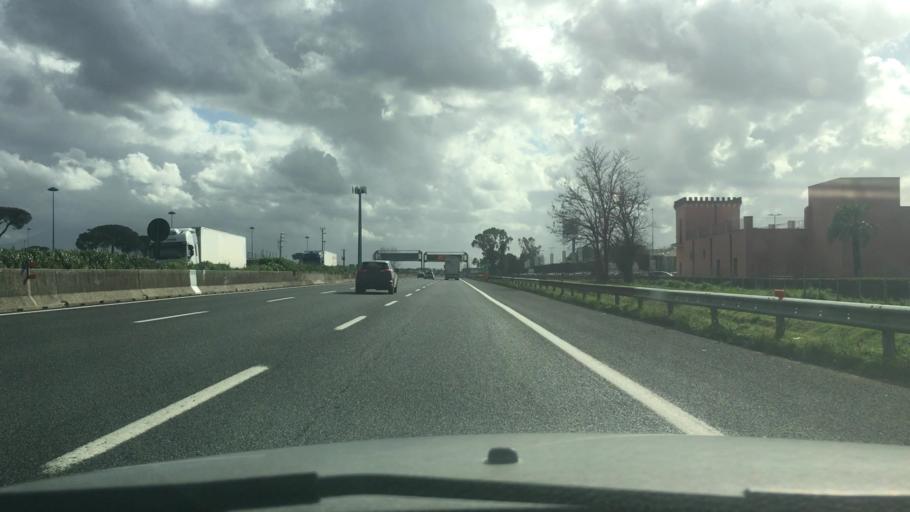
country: IT
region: Campania
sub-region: Provincia di Caserta
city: Marcianise
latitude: 41.0093
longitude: 14.3230
